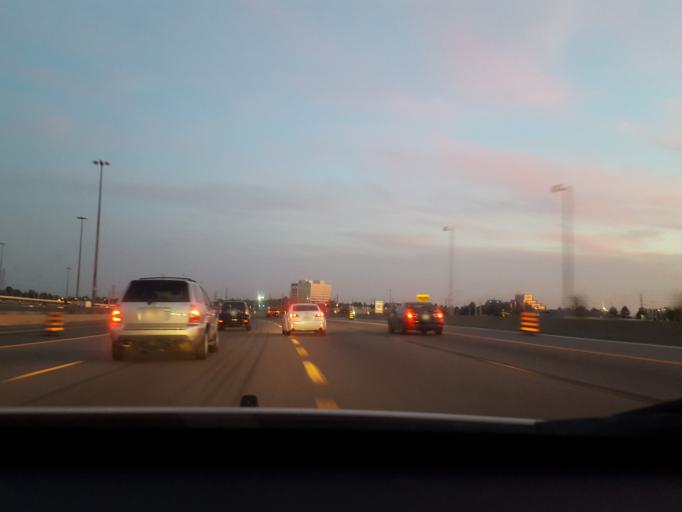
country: CA
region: Ontario
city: Etobicoke
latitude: 43.6754
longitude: -79.5924
